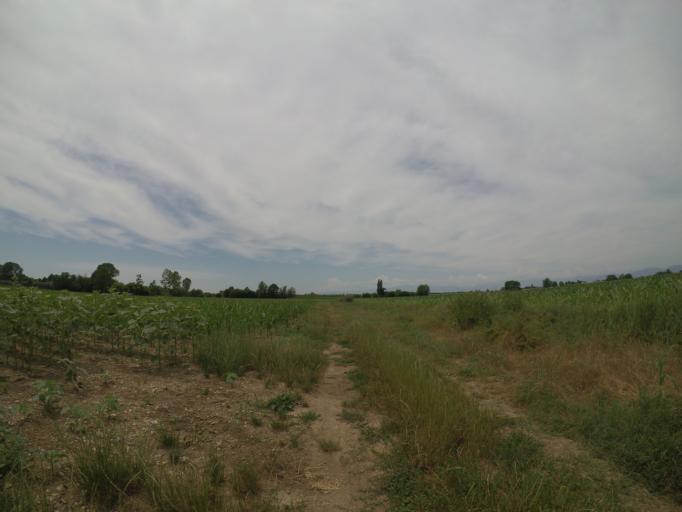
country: IT
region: Friuli Venezia Giulia
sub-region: Provincia di Udine
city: Bertiolo
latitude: 45.9329
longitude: 13.0465
